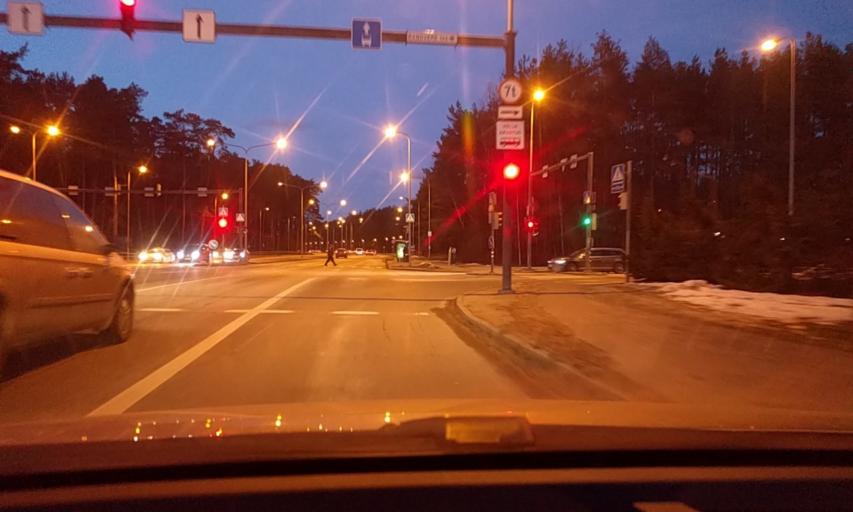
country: EE
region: Harju
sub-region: Viimsi vald
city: Viimsi
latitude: 59.4740
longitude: 24.8375
